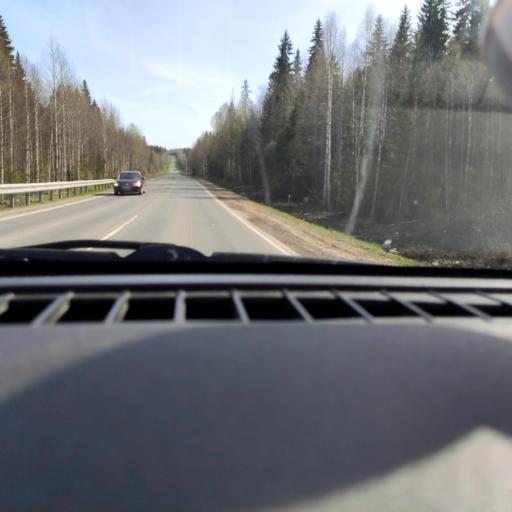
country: RU
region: Perm
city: Perm
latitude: 58.2389
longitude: 56.1589
